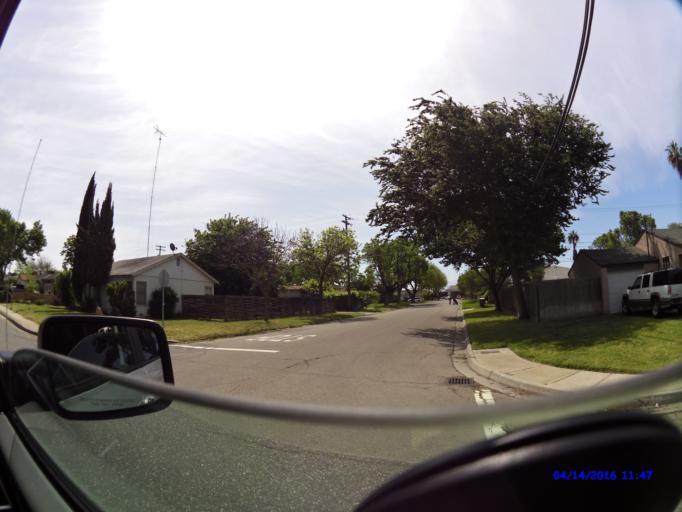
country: US
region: California
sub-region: Stanislaus County
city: Bystrom
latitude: 37.6401
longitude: -120.9596
